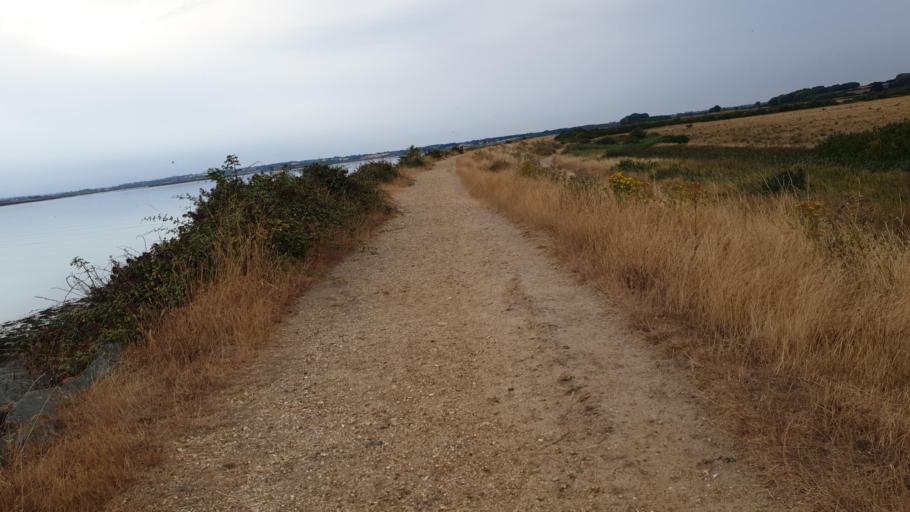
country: GB
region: England
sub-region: Essex
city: Brightlingsea
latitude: 51.8081
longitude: 1.0074
